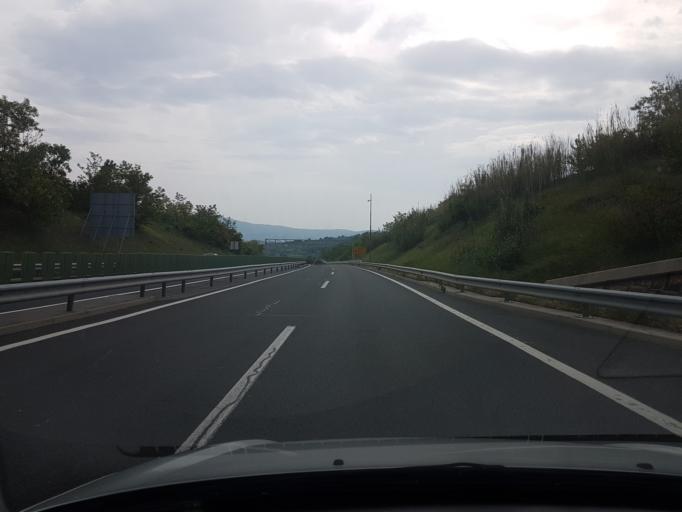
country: SI
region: Koper-Capodistria
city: Spodnje Skofije
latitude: 45.5699
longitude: 13.7869
